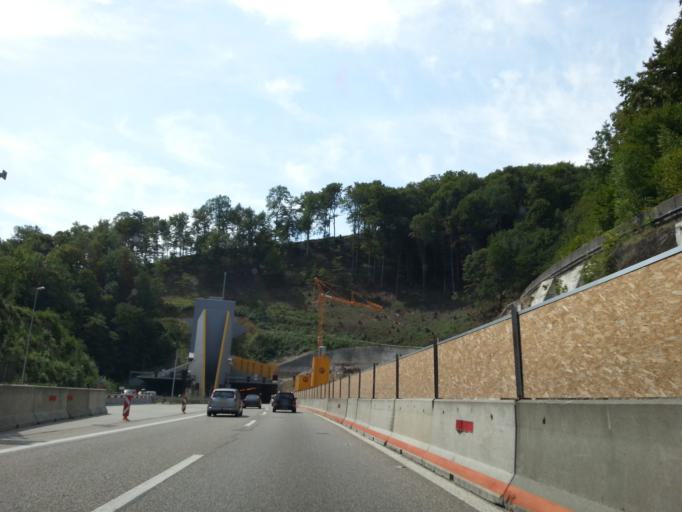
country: CH
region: Basel-Landschaft
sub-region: Bezirk Waldenburg
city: Diegten
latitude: 47.3802
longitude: 7.8163
